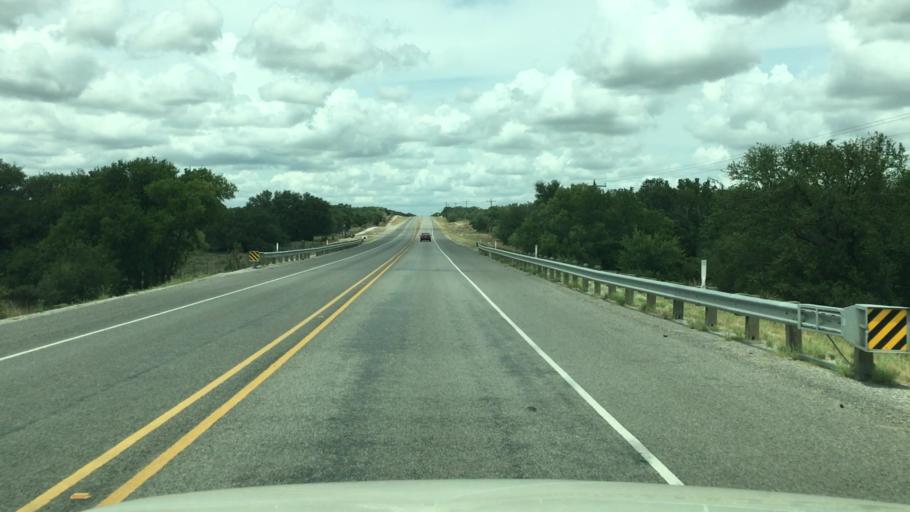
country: US
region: Texas
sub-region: McCulloch County
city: Brady
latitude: 31.0398
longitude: -99.2410
